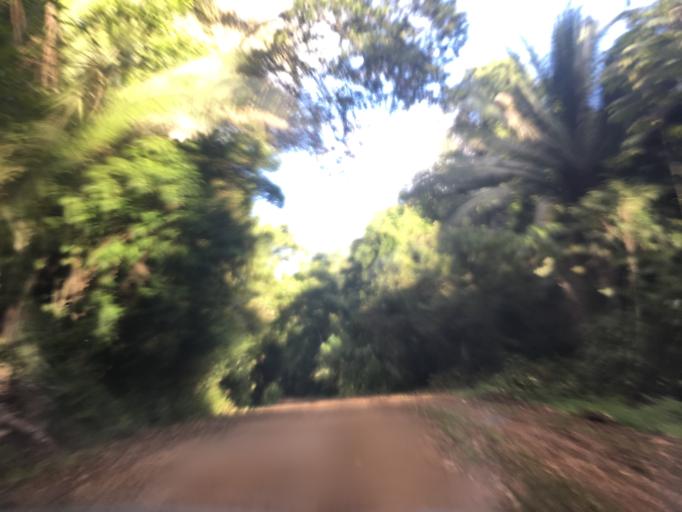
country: BZ
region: Stann Creek
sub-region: Dangriga
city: Dangriga
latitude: 16.7948
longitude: -88.4268
